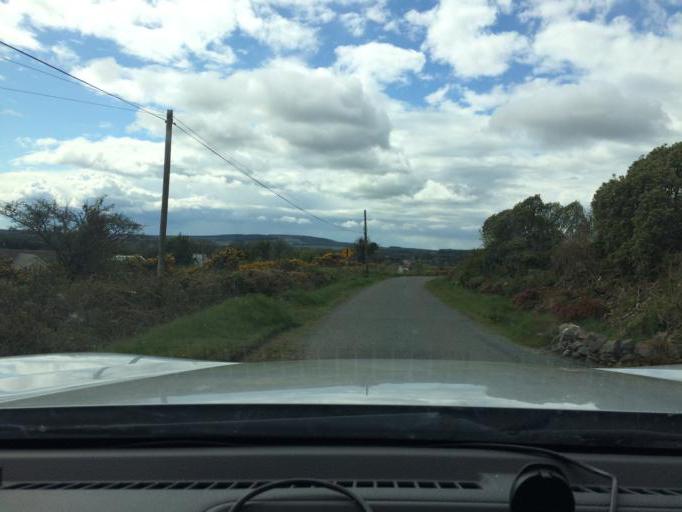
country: IE
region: Munster
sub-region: Waterford
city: Dungarvan
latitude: 52.0417
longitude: -7.6441
